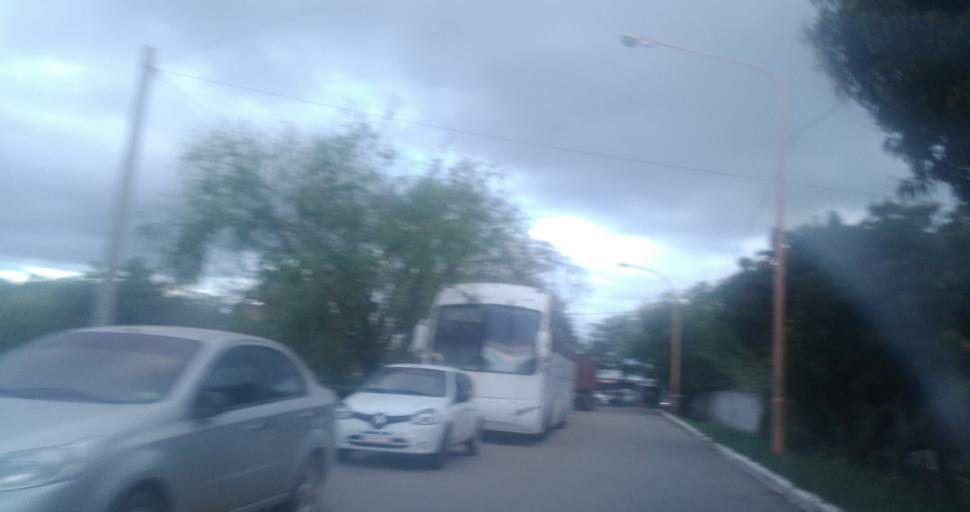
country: AR
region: Chaco
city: Resistencia
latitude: -27.4559
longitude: -58.9754
